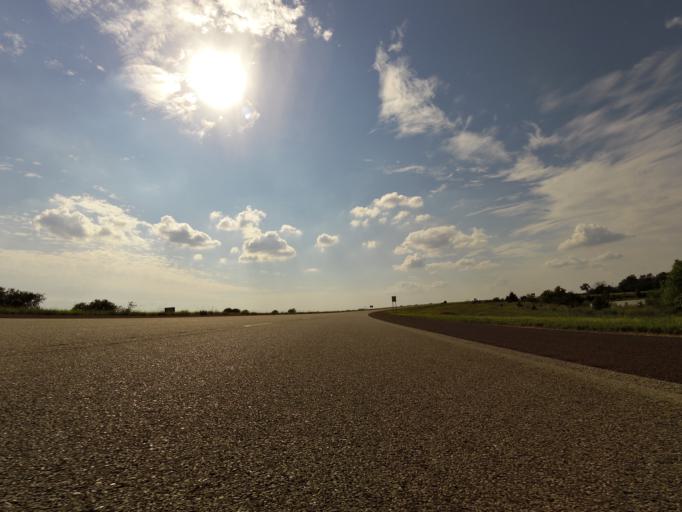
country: US
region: Kansas
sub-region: Reno County
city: Haven
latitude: 37.9369
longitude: -97.8747
